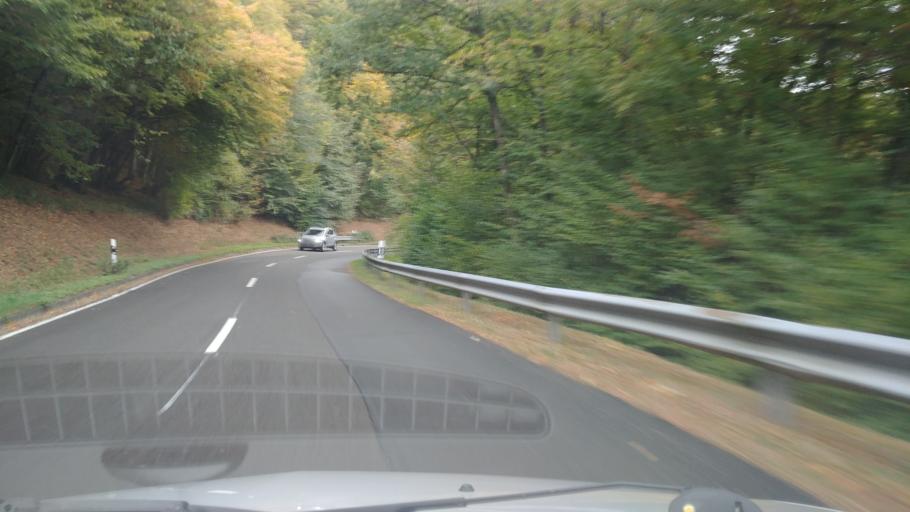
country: DE
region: Rheinland-Pfalz
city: Horath
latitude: 49.8038
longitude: 6.9861
